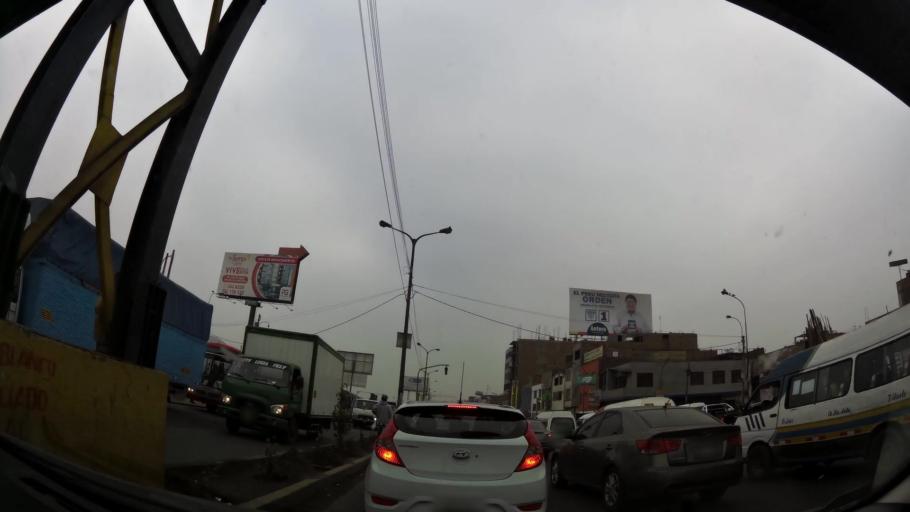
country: PE
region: Lima
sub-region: Lima
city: Vitarte
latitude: -12.0374
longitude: -76.9314
